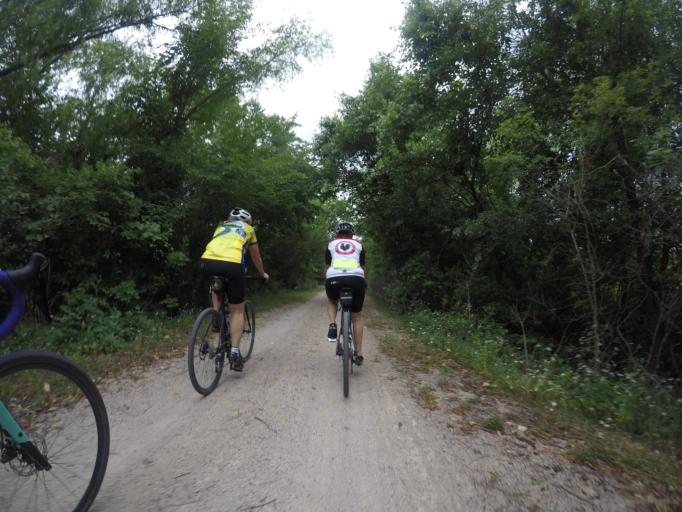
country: US
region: Kansas
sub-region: Anderson County
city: Garnett
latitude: 38.2571
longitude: -95.2510
